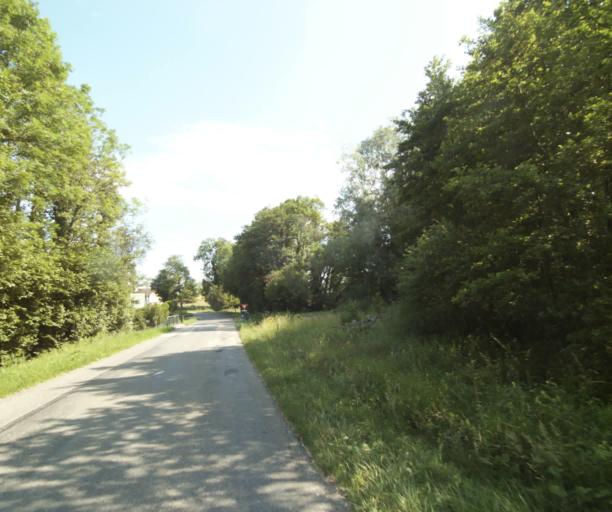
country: FR
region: Rhone-Alpes
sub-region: Departement de la Haute-Savoie
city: Allinges
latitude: 46.3330
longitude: 6.4926
